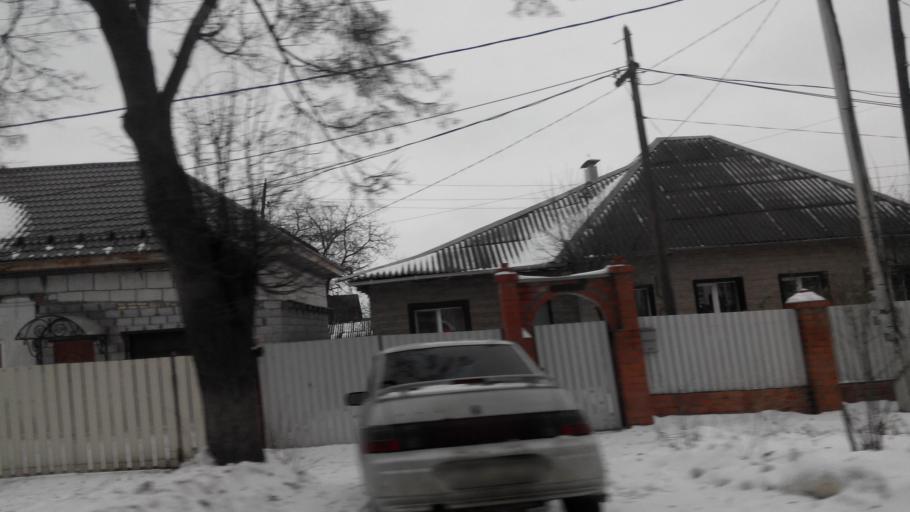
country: RU
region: Tula
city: Uzlovaya
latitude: 53.9817
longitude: 38.1909
